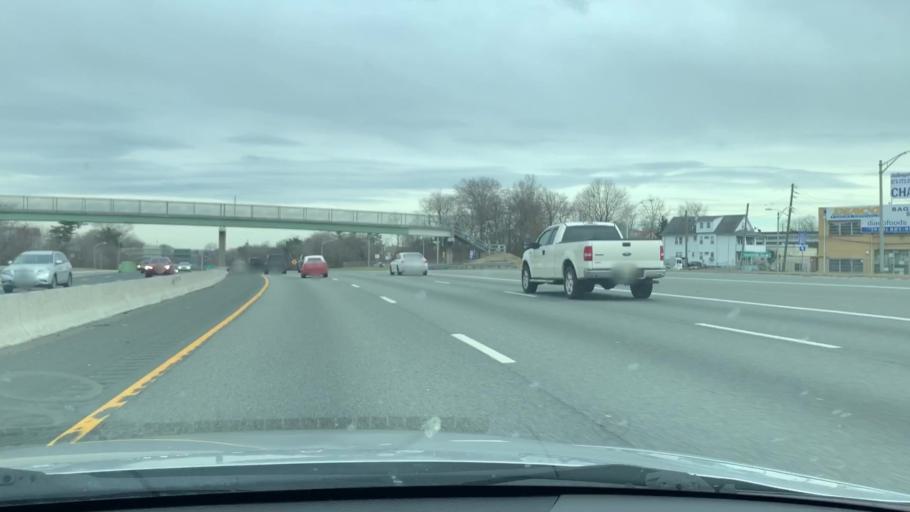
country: US
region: New Jersey
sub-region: Passaic County
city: Paterson
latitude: 40.9013
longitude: -74.1548
